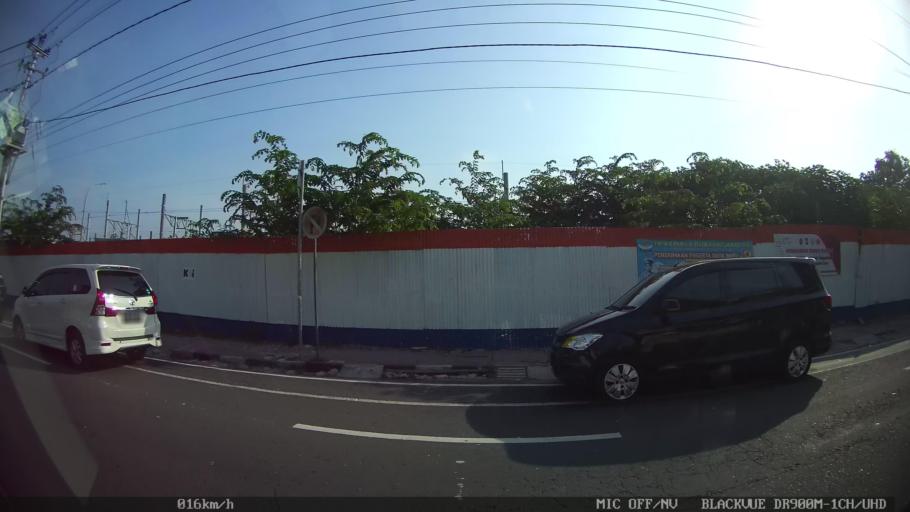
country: ID
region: Daerah Istimewa Yogyakarta
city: Yogyakarta
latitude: -7.7895
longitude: 110.3618
